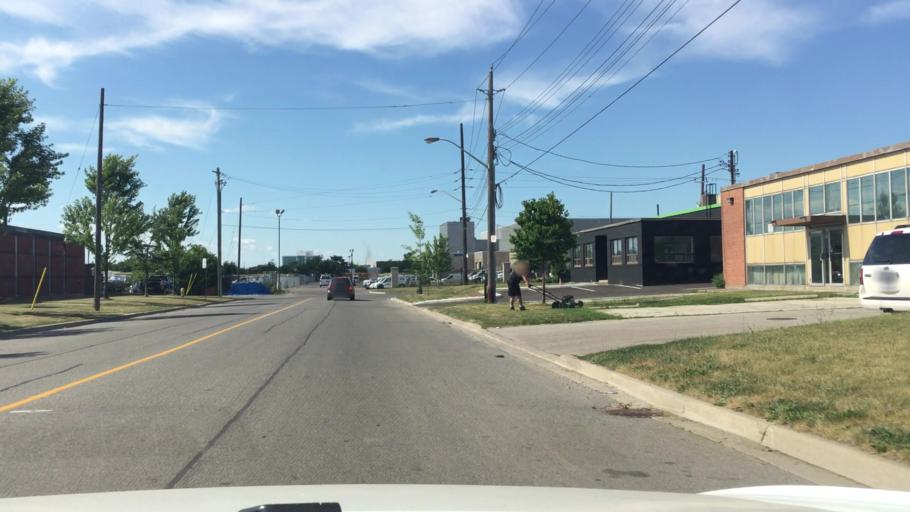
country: CA
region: Ontario
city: Scarborough
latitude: 43.7544
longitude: -79.2911
